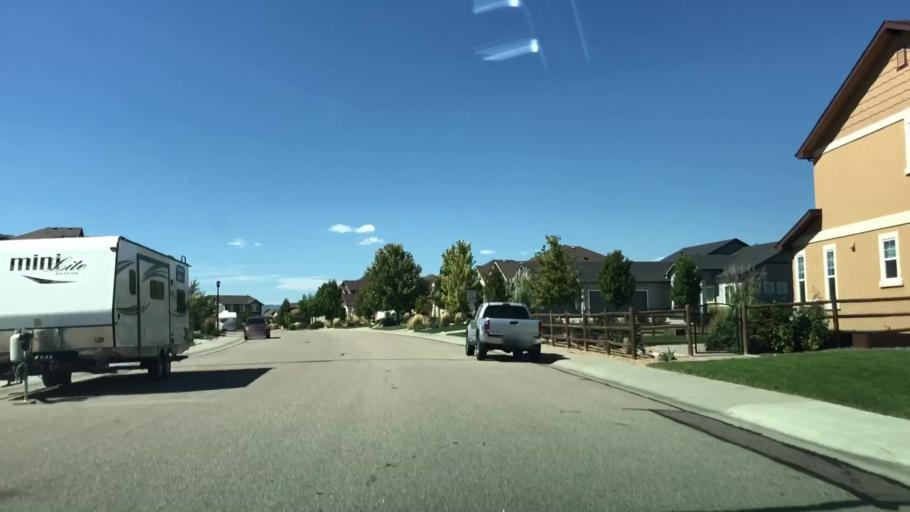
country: US
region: Colorado
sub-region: Weld County
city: Windsor
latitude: 40.4554
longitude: -104.9507
